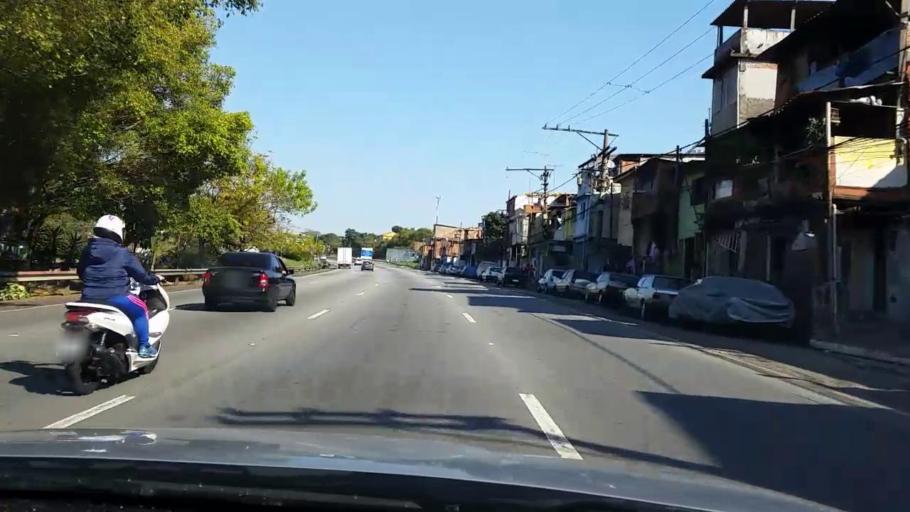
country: BR
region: Sao Paulo
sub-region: Diadema
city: Diadema
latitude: -23.6521
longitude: -46.6341
